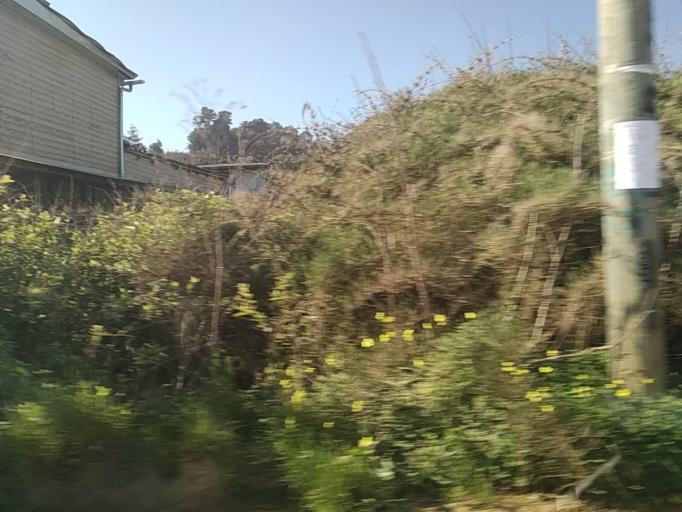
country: CL
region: Valparaiso
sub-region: San Antonio Province
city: El Tabo
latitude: -33.4578
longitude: -71.6581
